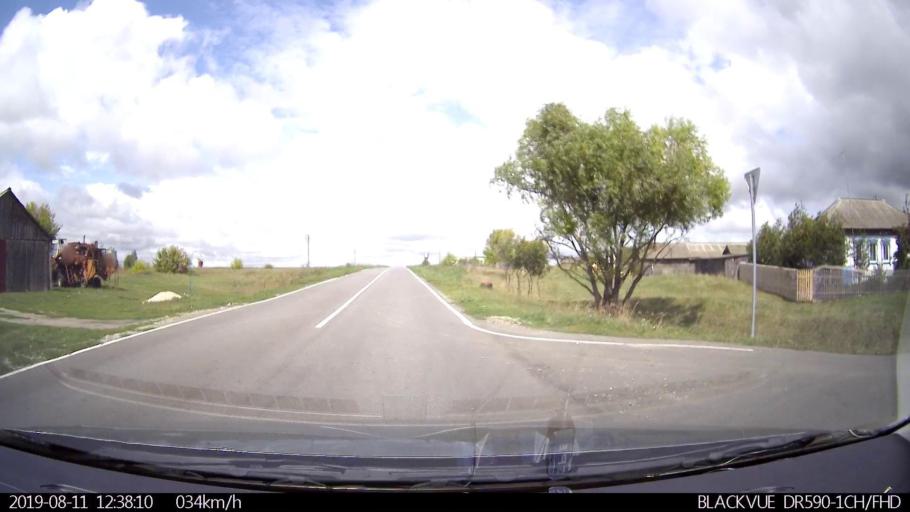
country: RU
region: Ulyanovsk
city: Ignatovka
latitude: 53.8254
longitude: 47.8083
